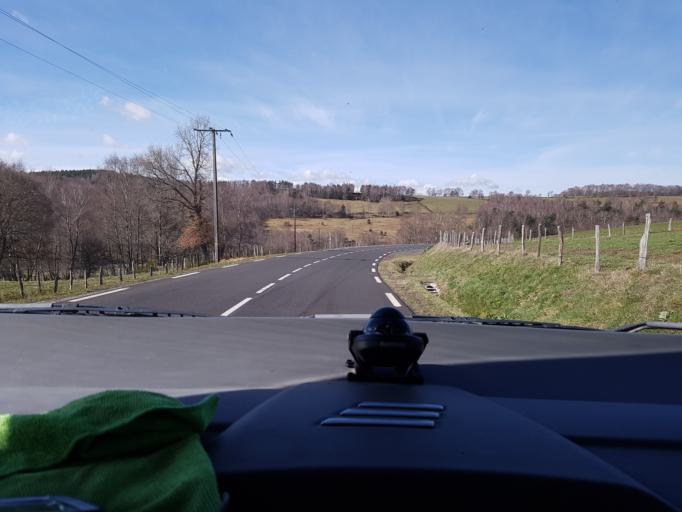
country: FR
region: Auvergne
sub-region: Departement du Cantal
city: Chaudes-Aigues
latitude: 44.8158
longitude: 2.9756
